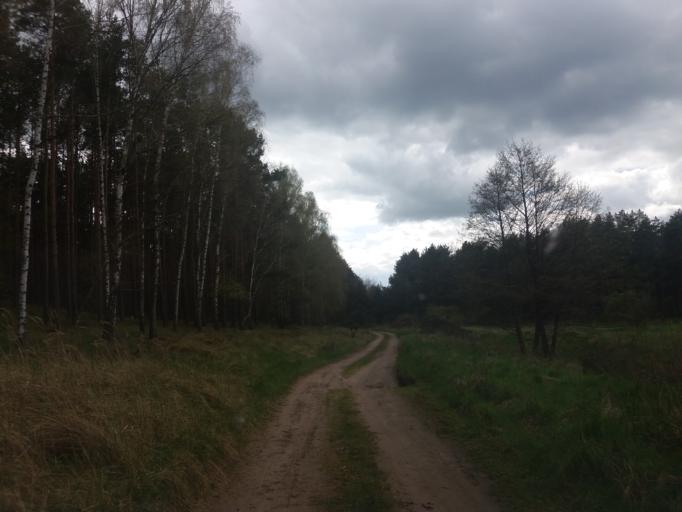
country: PL
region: West Pomeranian Voivodeship
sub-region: Powiat choszczenski
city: Recz
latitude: 53.2406
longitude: 15.5252
